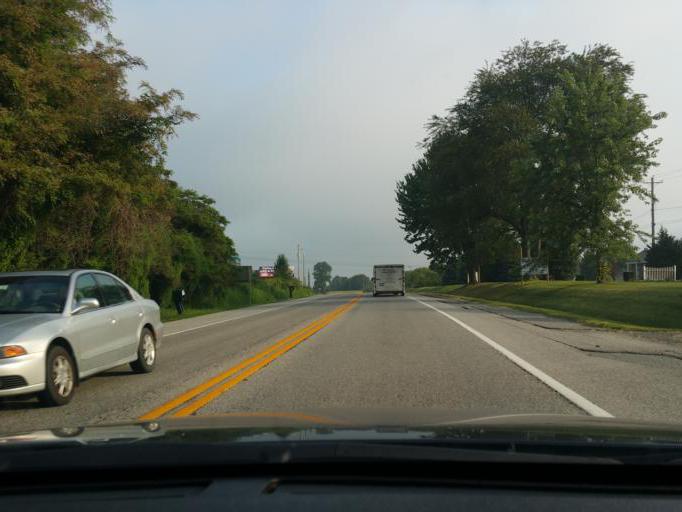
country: US
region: Maryland
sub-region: Cecil County
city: Rising Sun
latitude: 39.6765
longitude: -76.0737
